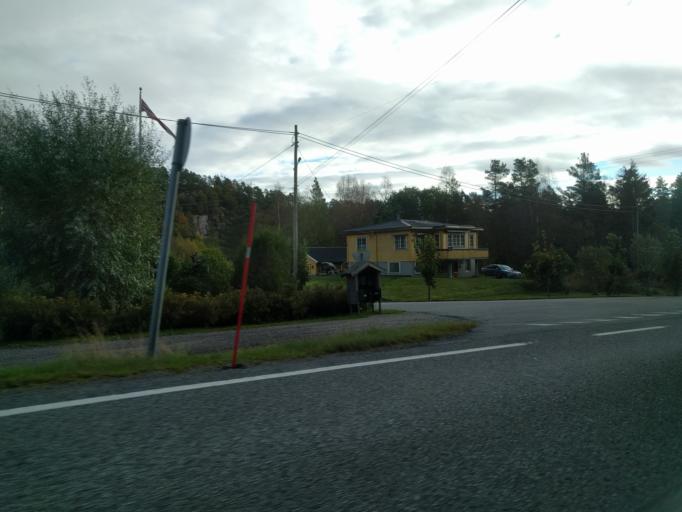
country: NO
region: Vest-Agder
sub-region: Kristiansand
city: Strai
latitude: 58.2488
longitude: 7.8685
